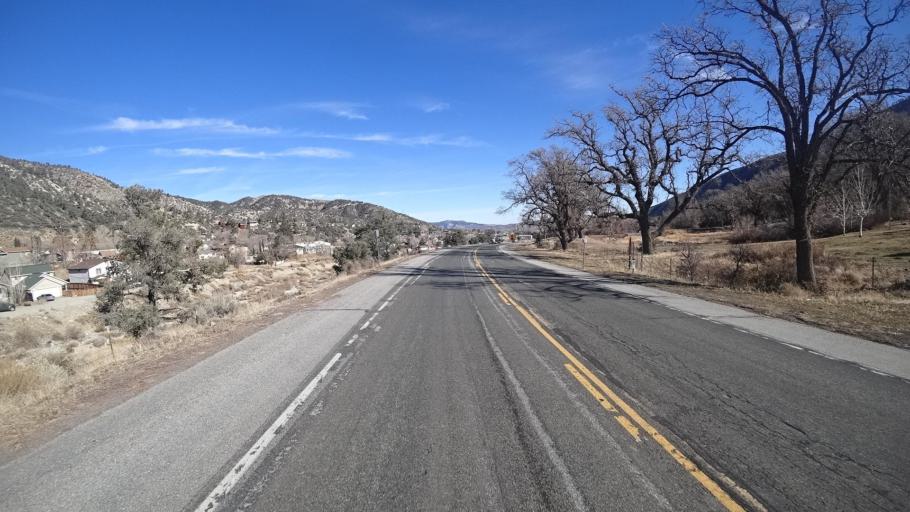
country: US
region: California
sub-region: Kern County
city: Frazier Park
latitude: 34.8213
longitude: -118.9491
